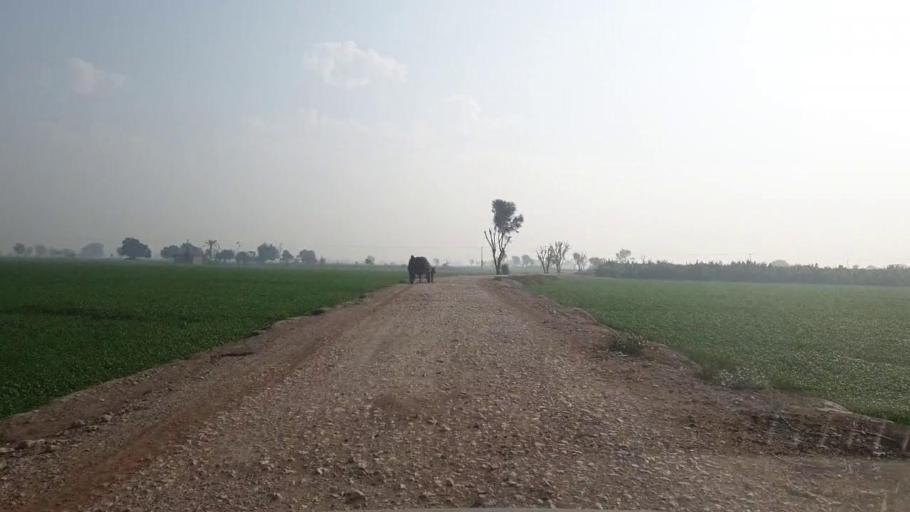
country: PK
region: Sindh
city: Hala
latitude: 25.8597
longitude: 68.4307
